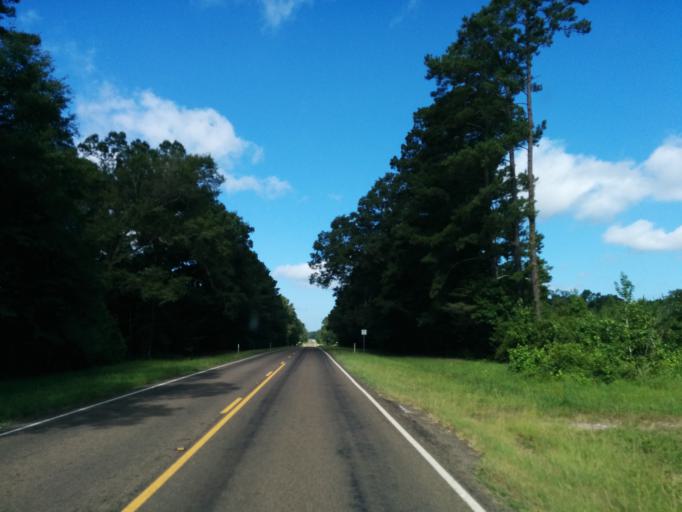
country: US
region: Texas
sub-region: San Augustine County
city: San Augustine
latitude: 31.4116
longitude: -94.0092
